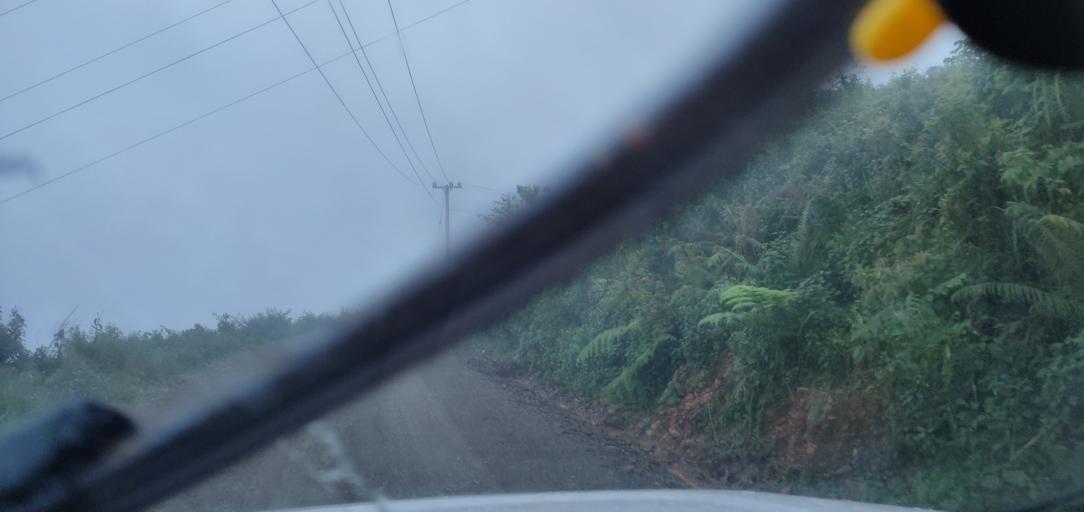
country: LA
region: Phongsali
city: Phongsali
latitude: 21.3977
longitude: 102.2239
